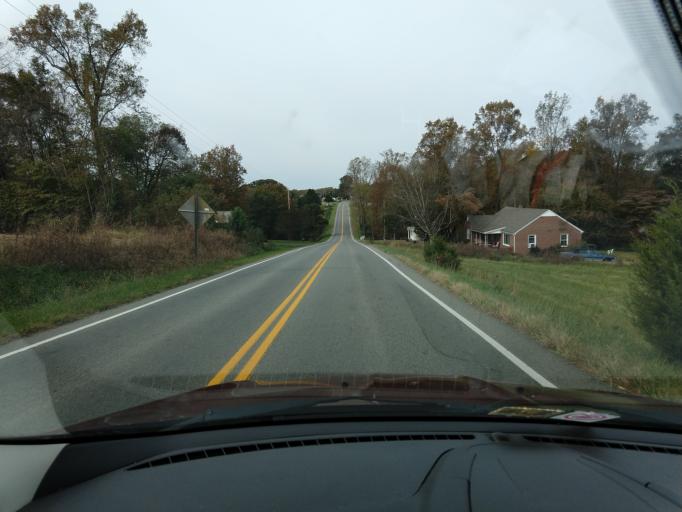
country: US
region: Virginia
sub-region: Franklin County
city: Union Hall
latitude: 36.9928
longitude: -79.6801
